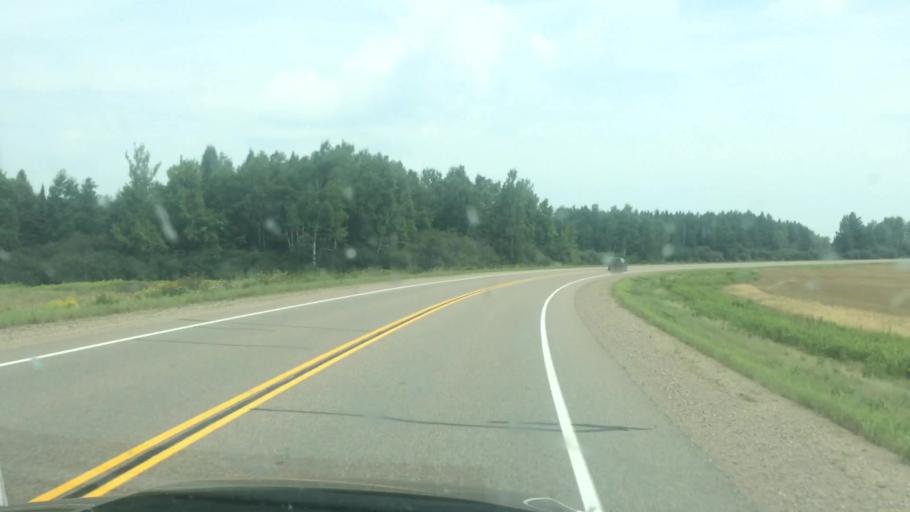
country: US
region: Wisconsin
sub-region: Langlade County
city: Antigo
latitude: 45.1495
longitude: -89.1845
